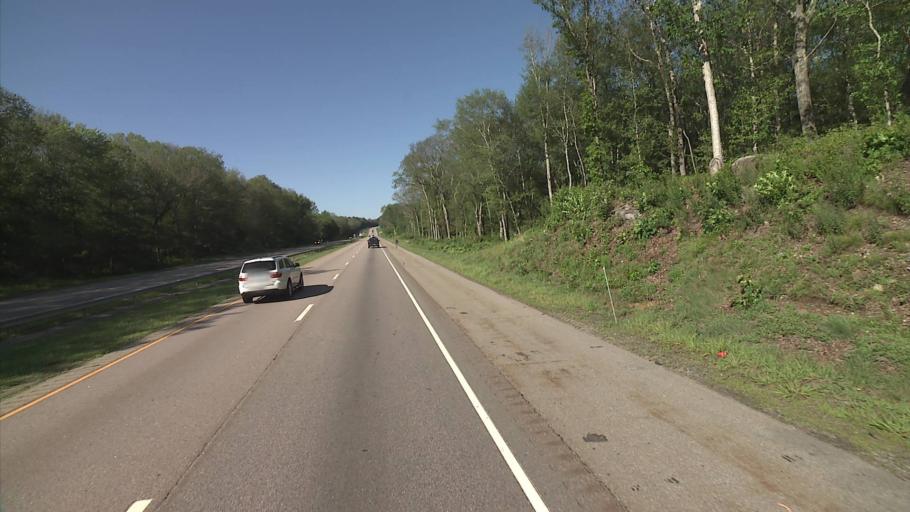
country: US
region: Connecticut
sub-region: New London County
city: Oxoboxo River
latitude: 41.4120
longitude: -72.1411
